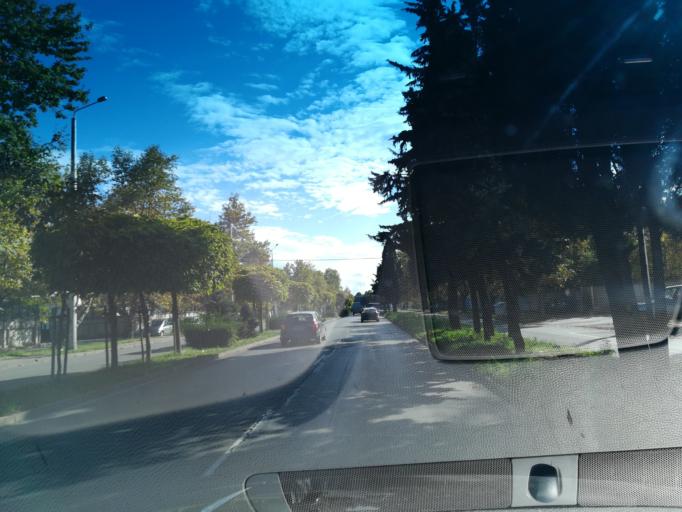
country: BG
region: Stara Zagora
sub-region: Obshtina Stara Zagora
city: Stara Zagora
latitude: 42.4118
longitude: 25.6391
